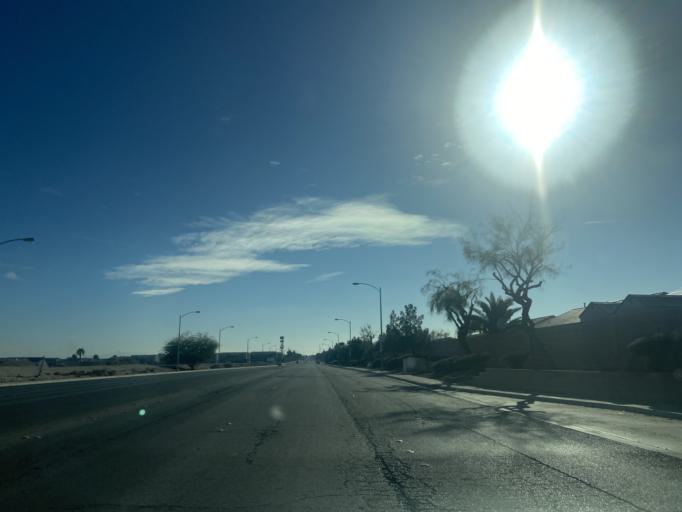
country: US
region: Nevada
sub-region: Clark County
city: North Las Vegas
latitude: 36.2464
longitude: -115.1801
